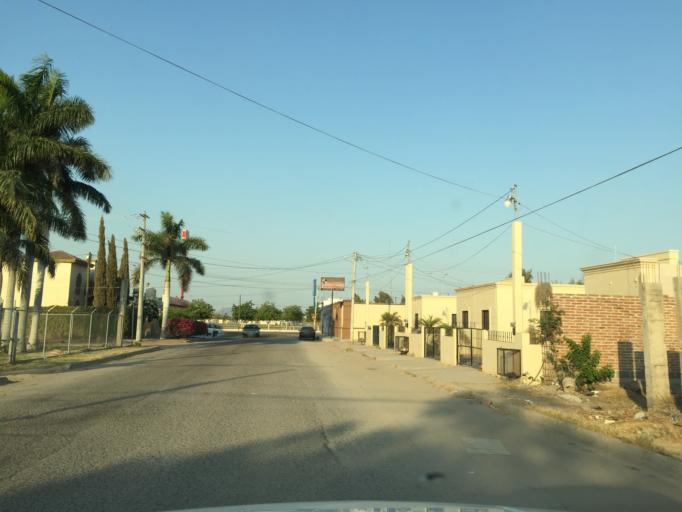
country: MX
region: Sonora
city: Navojoa
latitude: 27.0564
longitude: -109.4565
